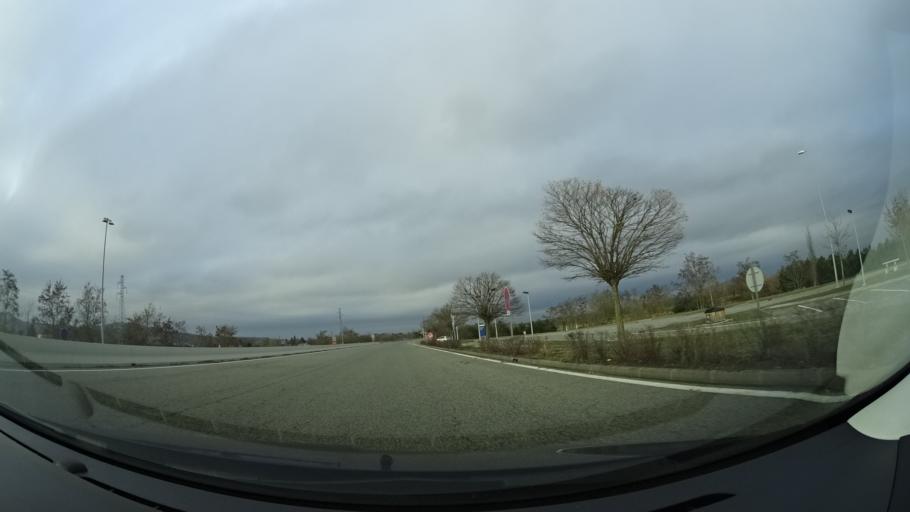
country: FR
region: Midi-Pyrenees
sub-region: Departement de l'Ariege
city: Pamiers
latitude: 43.1553
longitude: 1.6159
